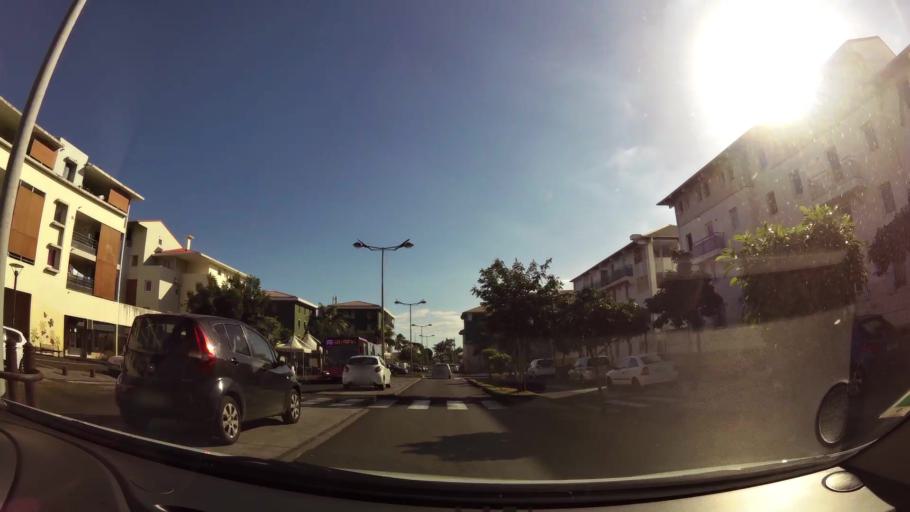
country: RE
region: Reunion
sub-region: Reunion
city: Saint-Louis
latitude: -21.2858
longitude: 55.4179
